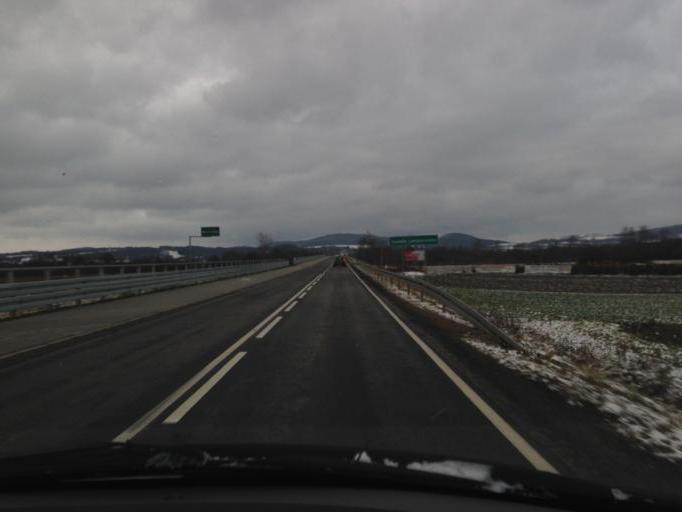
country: PL
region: Lesser Poland Voivodeship
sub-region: Powiat tarnowski
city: Zakliczyn
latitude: 49.8700
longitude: 20.8112
